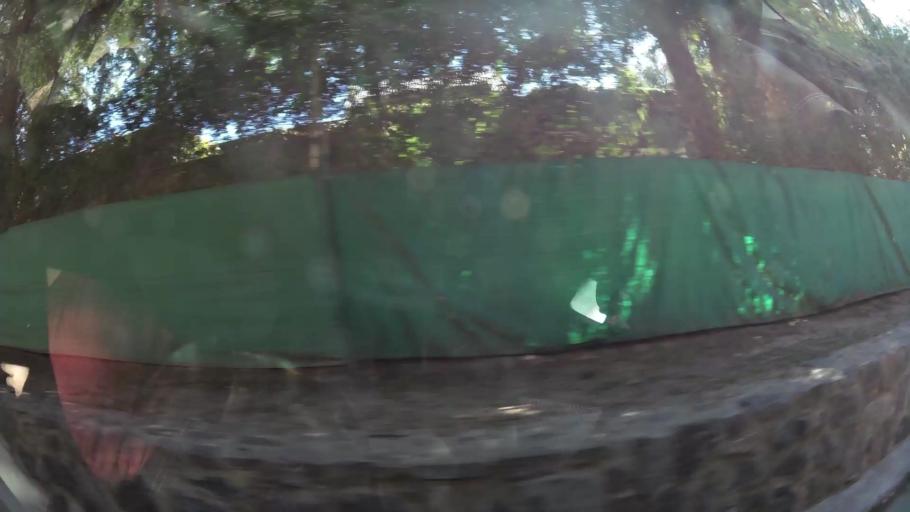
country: AR
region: Cordoba
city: Villa Allende
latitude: -31.2911
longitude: -64.2856
